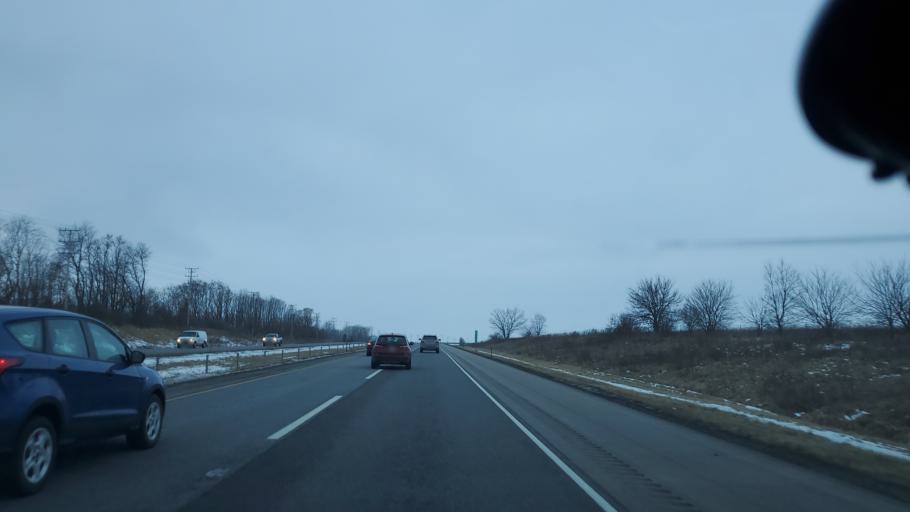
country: US
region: Illinois
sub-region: Kane County
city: Sugar Grove
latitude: 41.8007
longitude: -88.4144
